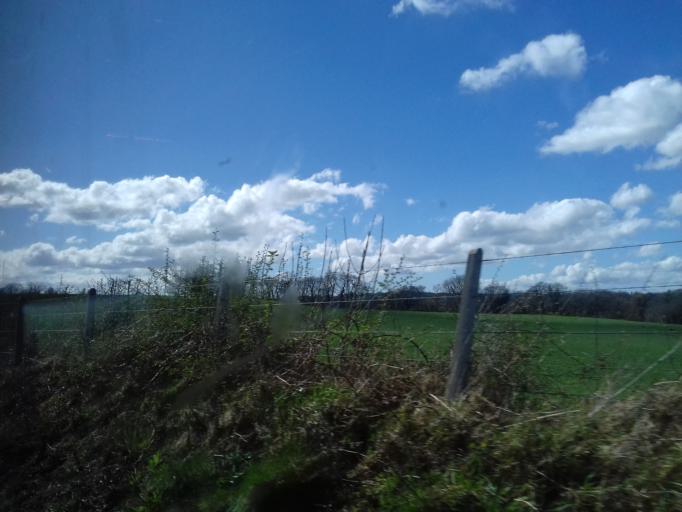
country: IE
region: Munster
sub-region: County Cork
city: Millstreet
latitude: 52.0827
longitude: -9.0368
